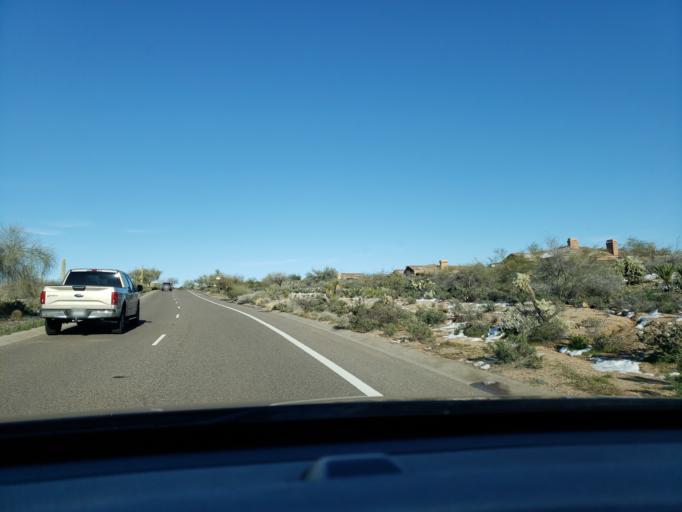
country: US
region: Arizona
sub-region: Maricopa County
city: Carefree
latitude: 33.8266
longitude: -111.8643
